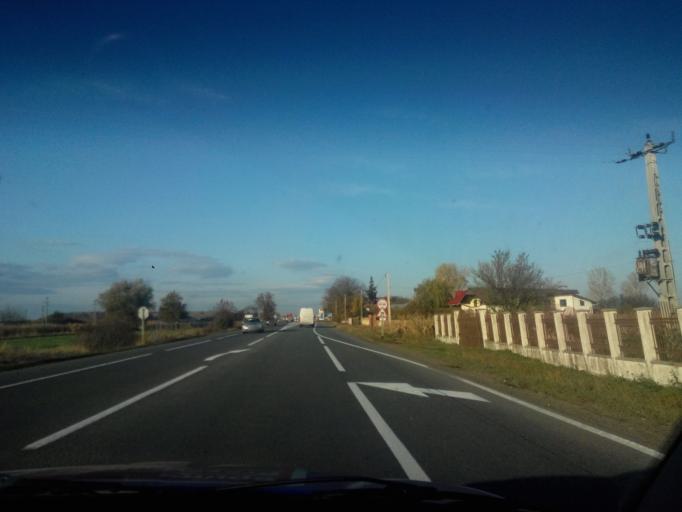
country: RO
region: Neamt
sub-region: Comuna Secueni
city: Secueni
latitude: 46.8551
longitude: 26.8867
